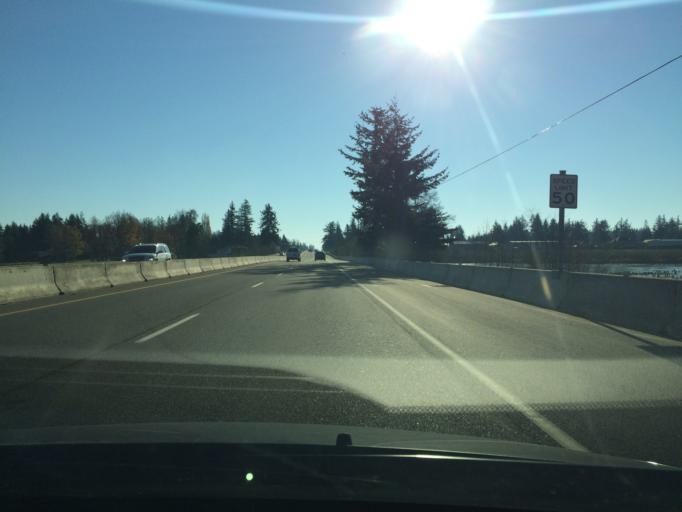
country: US
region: Washington
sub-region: Whatcom County
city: Lynden
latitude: 48.9047
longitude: -122.4856
